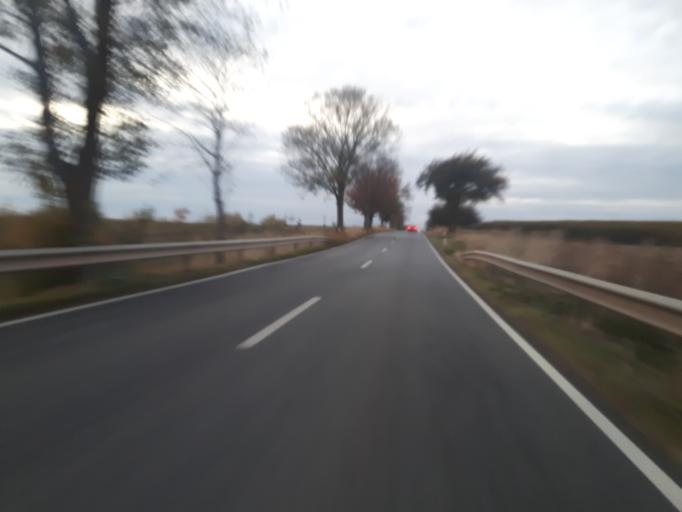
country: DE
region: Rheinland-Pfalz
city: Ober-Florsheim
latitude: 49.6774
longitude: 8.1713
